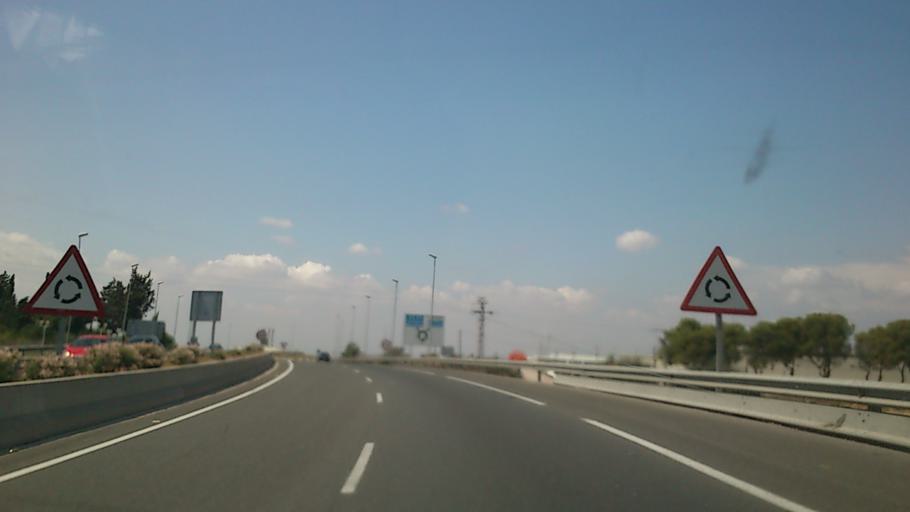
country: ES
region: Valencia
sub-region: Provincia de Valencia
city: Museros
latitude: 39.5940
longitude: -0.3617
